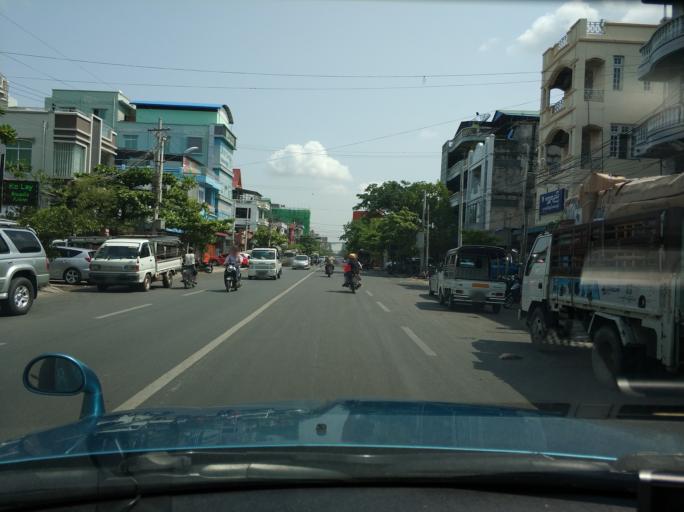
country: MM
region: Mandalay
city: Mandalay
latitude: 21.9682
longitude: 96.0803
